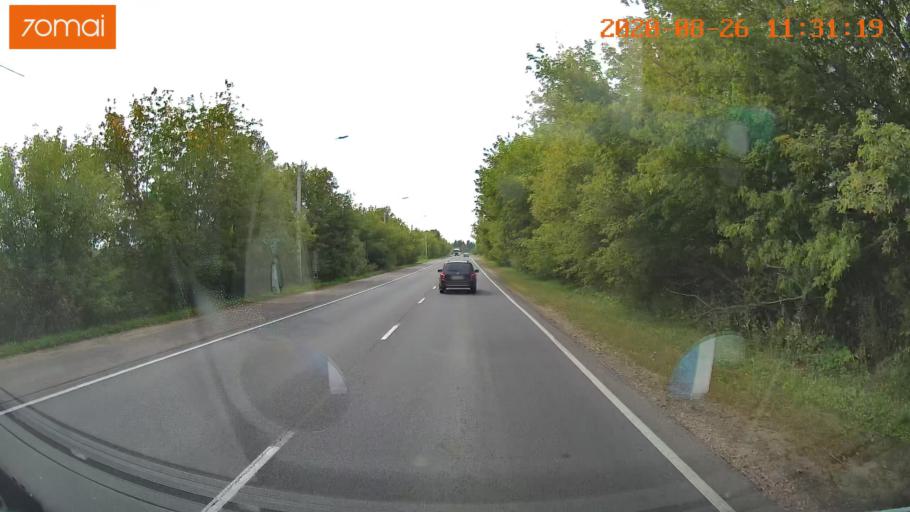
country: RU
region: Rjazan
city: Shilovo
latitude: 54.3075
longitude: 40.8748
